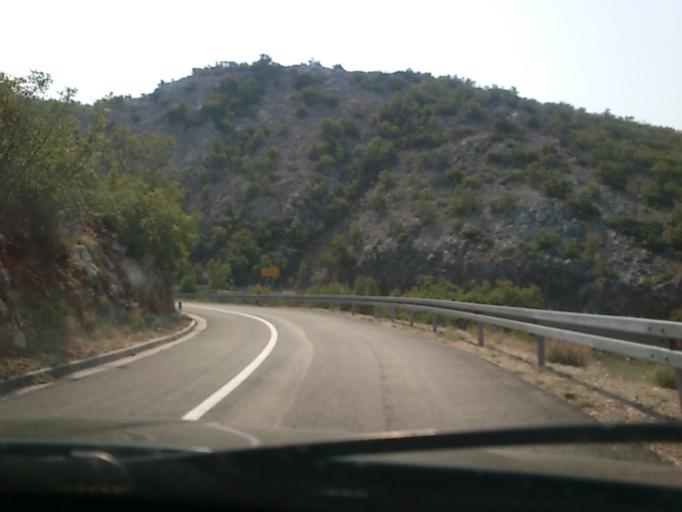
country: HR
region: Primorsko-Goranska
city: Banjol
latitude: 44.7089
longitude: 14.9035
